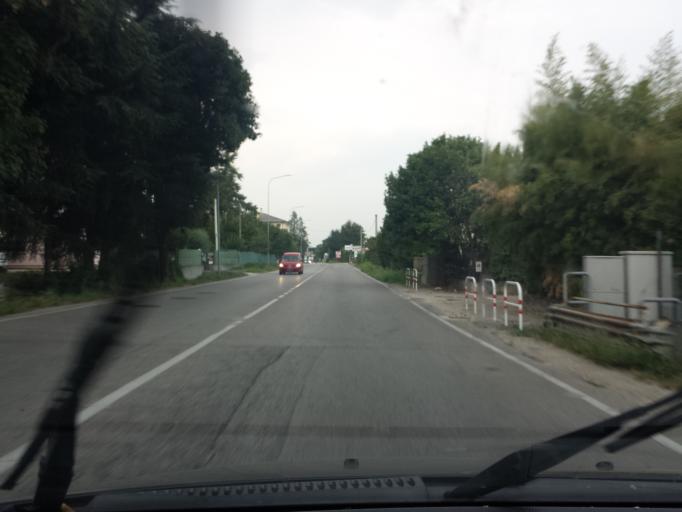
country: IT
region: Veneto
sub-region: Provincia di Vicenza
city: Monticello Conte Otto
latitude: 45.5825
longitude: 11.5537
